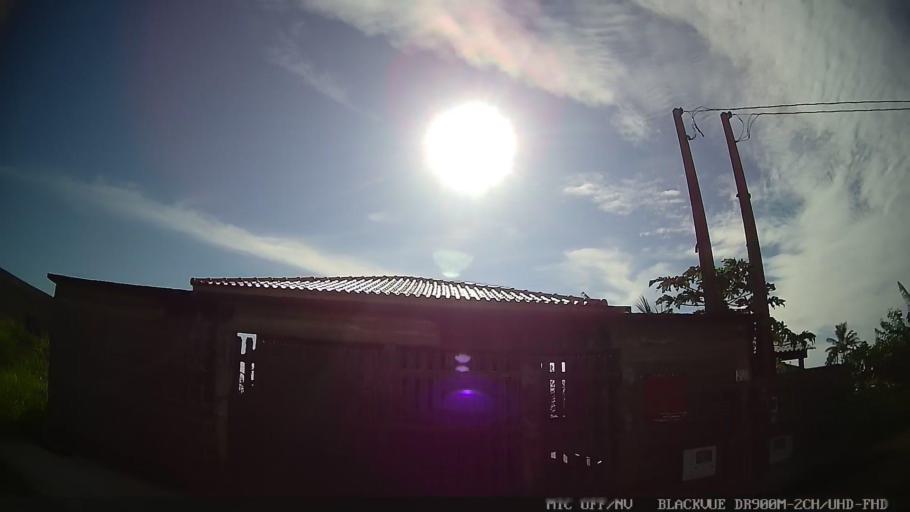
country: BR
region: Sao Paulo
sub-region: Iguape
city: Iguape
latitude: -24.7656
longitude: -47.5810
